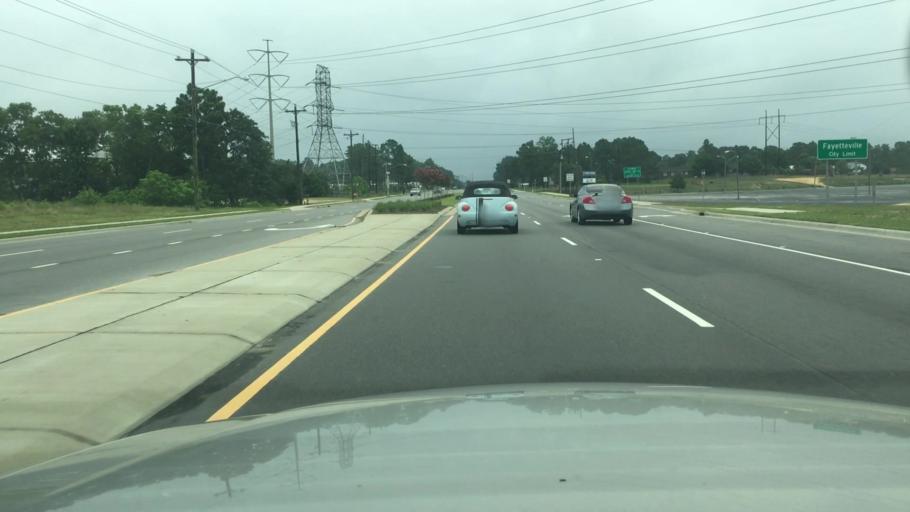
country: US
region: North Carolina
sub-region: Cumberland County
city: Hope Mills
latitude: 35.0075
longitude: -78.9128
